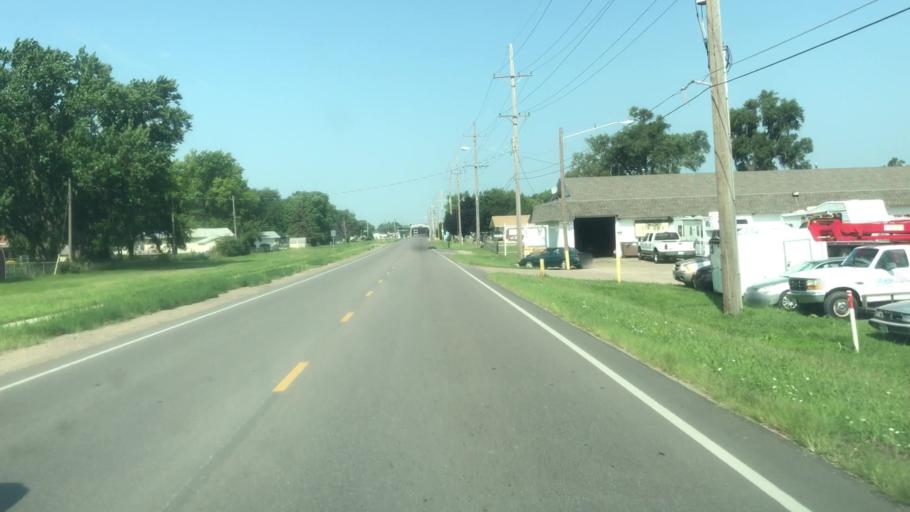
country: US
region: Nebraska
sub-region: Hall County
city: Grand Island
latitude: 40.9458
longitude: -98.3505
